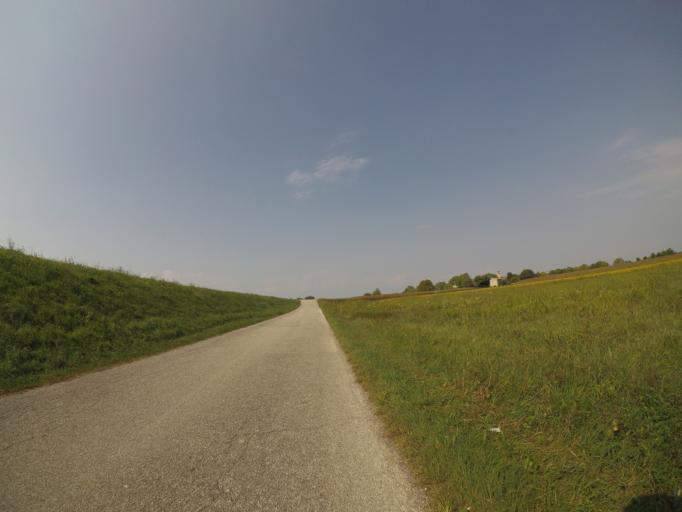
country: IT
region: Friuli Venezia Giulia
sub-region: Provincia di Udine
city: Camino al Tagliamento
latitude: 45.9133
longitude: 12.9290
